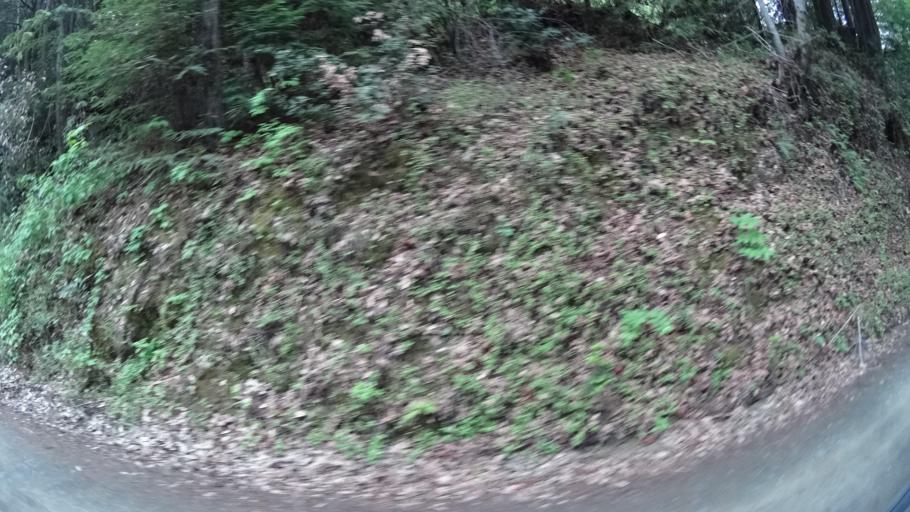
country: US
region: California
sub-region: Humboldt County
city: Redway
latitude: 40.3226
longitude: -123.8360
